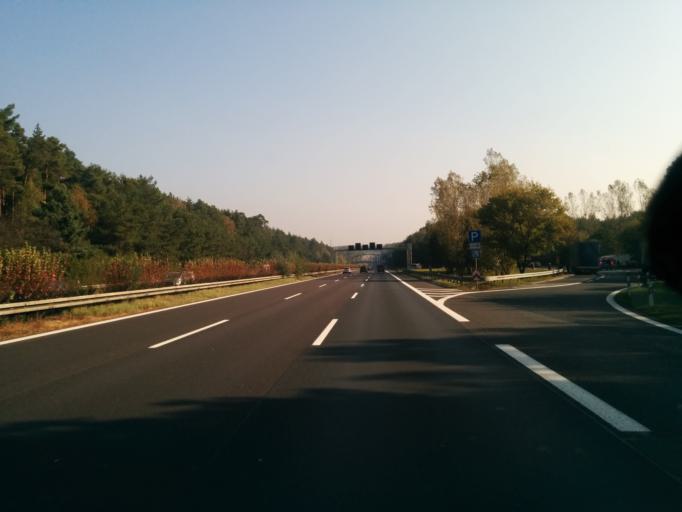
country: DE
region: Brandenburg
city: Beelitz
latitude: 52.2984
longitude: 12.9534
